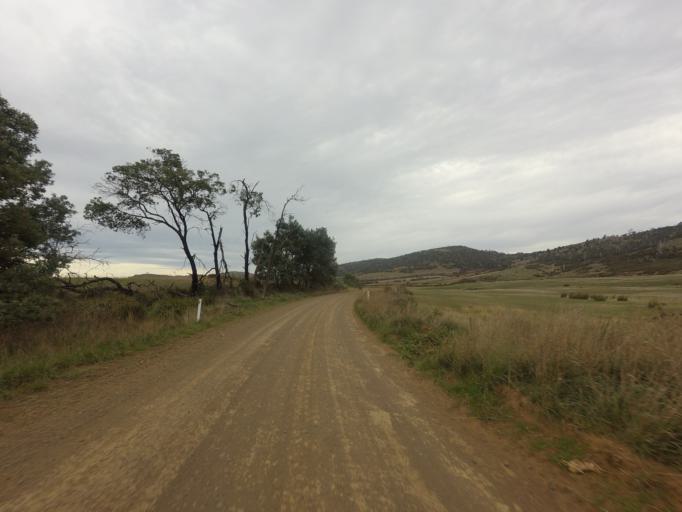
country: AU
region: Tasmania
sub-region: Derwent Valley
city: New Norfolk
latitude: -42.5385
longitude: 146.9451
